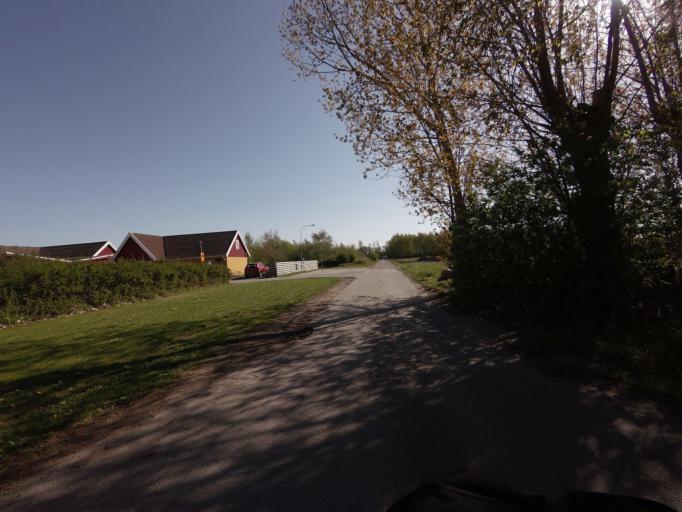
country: SE
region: Skane
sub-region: Landskrona
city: Asmundtorp
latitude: 55.8562
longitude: 12.9012
